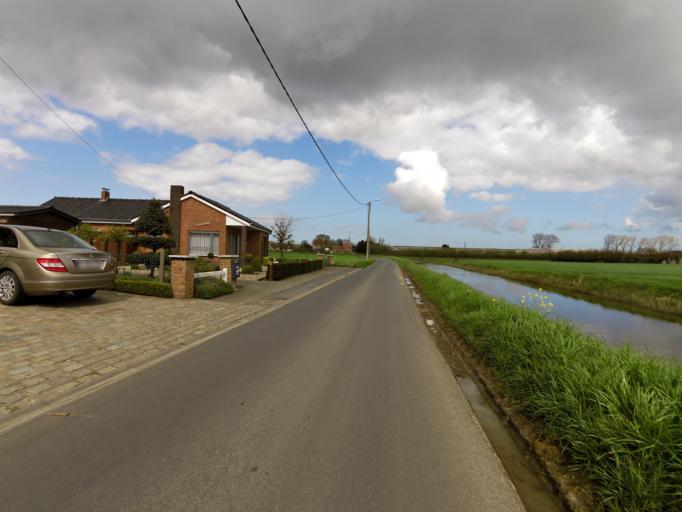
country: BE
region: Flanders
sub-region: Provincie West-Vlaanderen
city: Oudenburg
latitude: 51.1559
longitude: 2.9981
